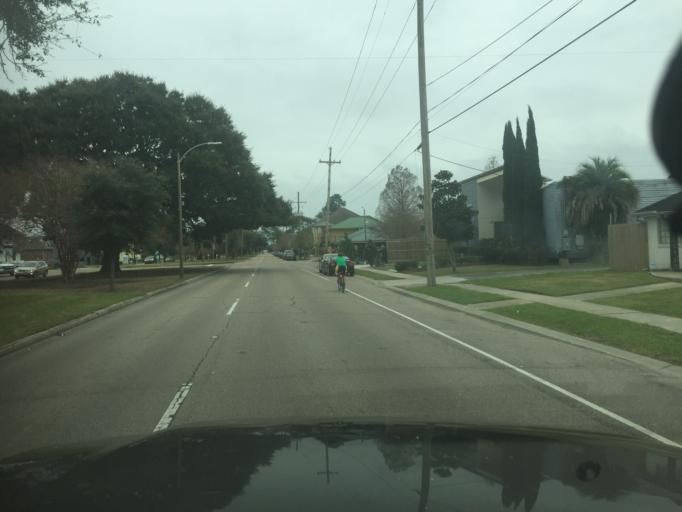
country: US
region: Louisiana
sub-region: Jefferson Parish
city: Metairie
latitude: 30.0051
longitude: -90.1134
